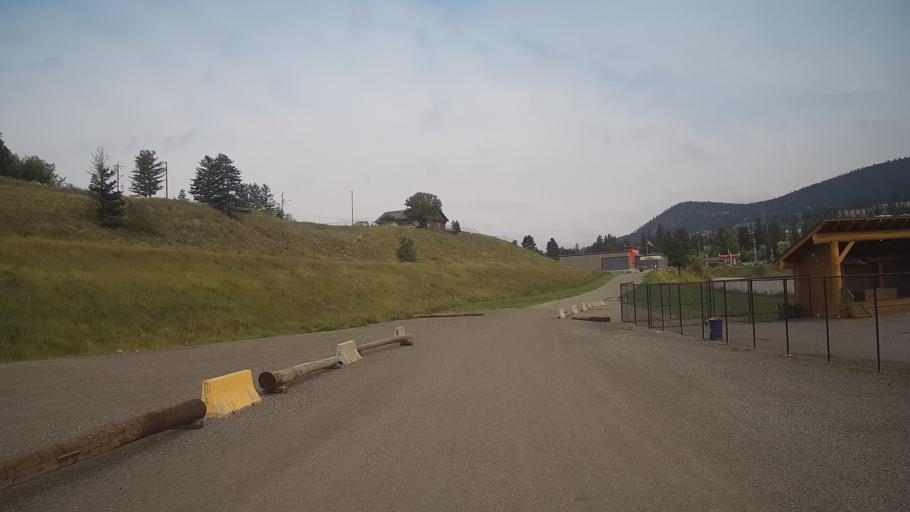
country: CA
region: British Columbia
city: Williams Lake
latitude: 52.1255
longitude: -122.1335
